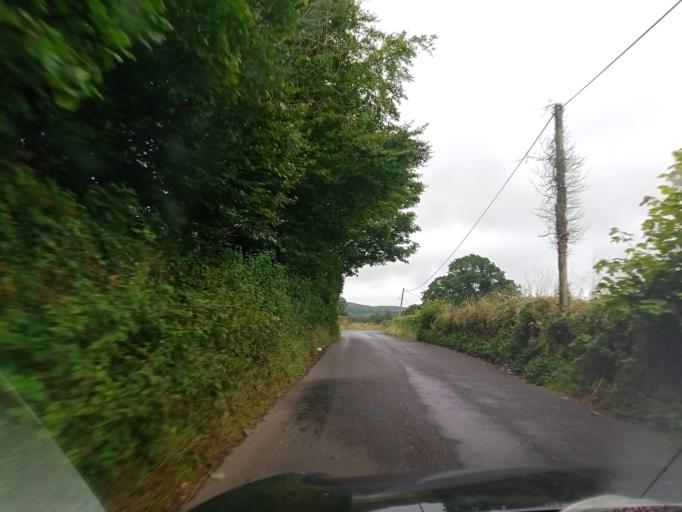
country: IE
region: Leinster
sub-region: Laois
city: Abbeyleix
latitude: 52.9281
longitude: -7.2804
